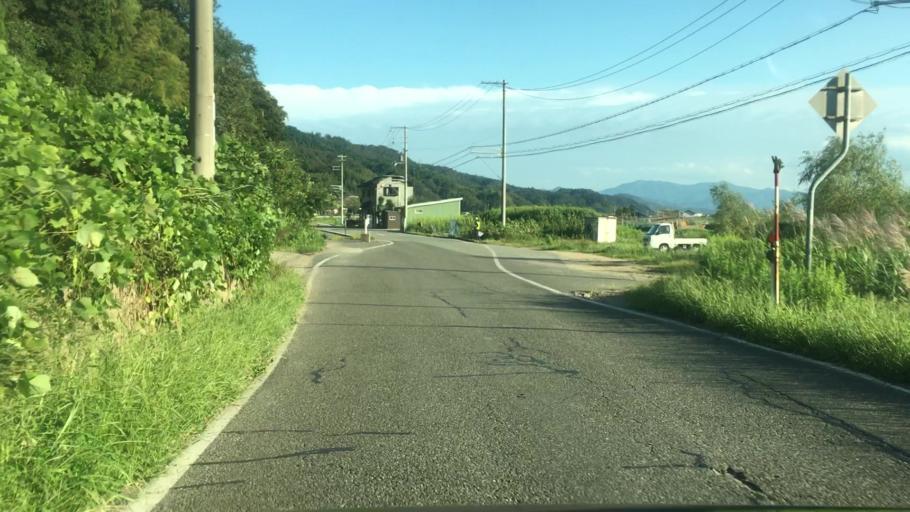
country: JP
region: Hyogo
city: Toyooka
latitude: 35.5869
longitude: 134.8051
